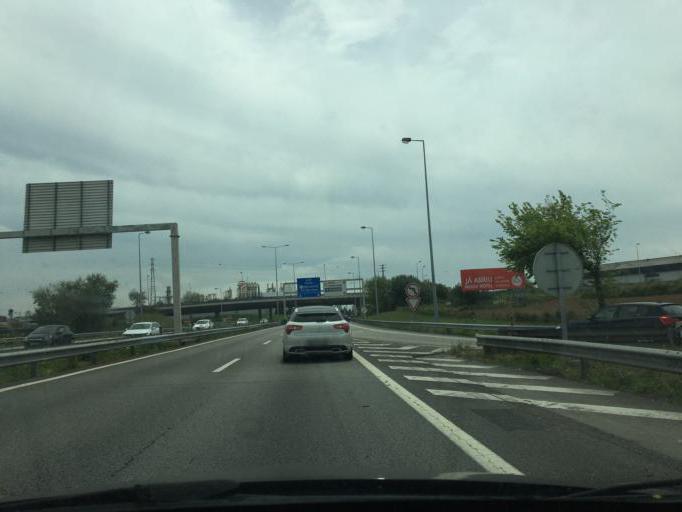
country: PT
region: Porto
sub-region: Matosinhos
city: Santa Cruz do Bispo
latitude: 41.2191
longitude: -8.6913
